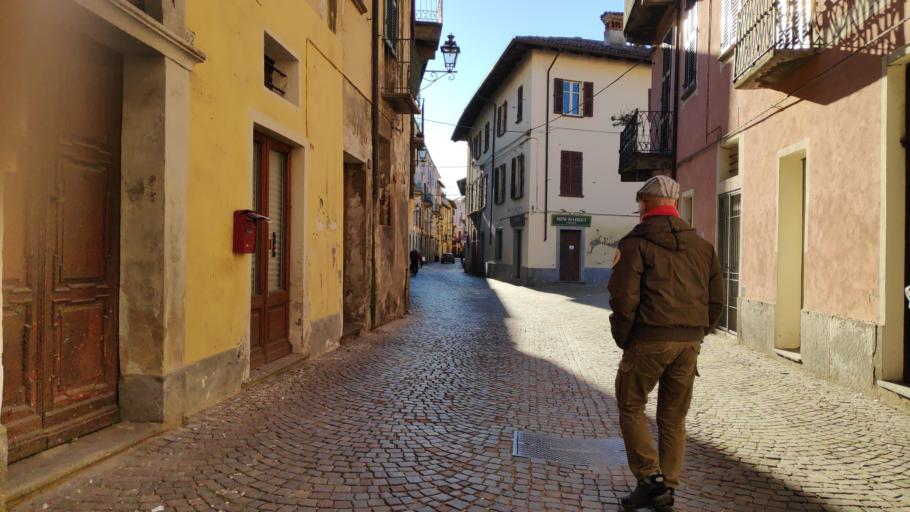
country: IT
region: Piedmont
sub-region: Provincia di Torino
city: Pinerolo
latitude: 44.8880
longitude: 7.3306
